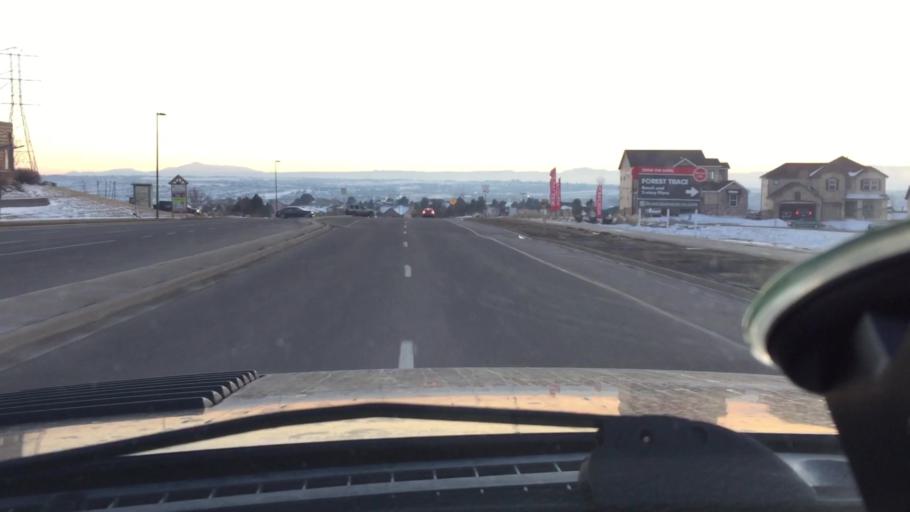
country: US
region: Colorado
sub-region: Douglas County
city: Parker
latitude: 39.5966
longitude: -104.7066
